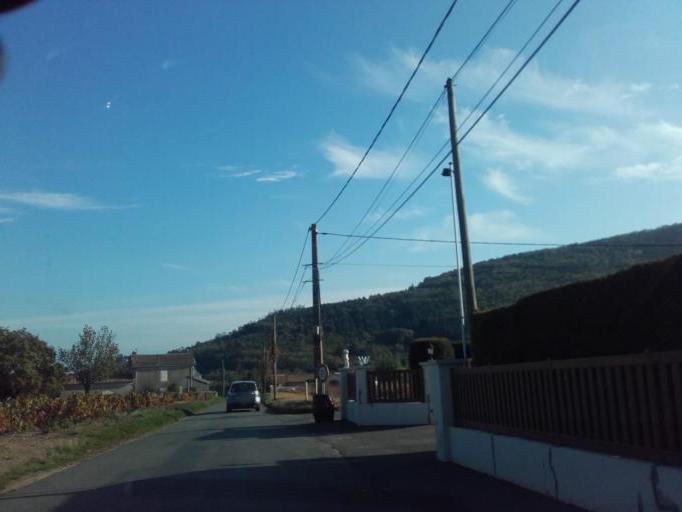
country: FR
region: Rhone-Alpes
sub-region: Departement du Rhone
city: Fleurie
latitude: 46.2335
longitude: 4.7053
